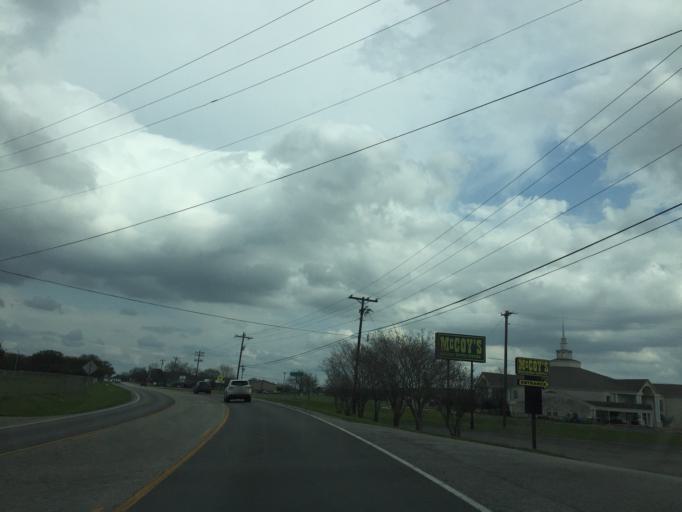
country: US
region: Texas
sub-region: Travis County
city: Manchaca
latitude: 30.1406
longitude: -97.8384
